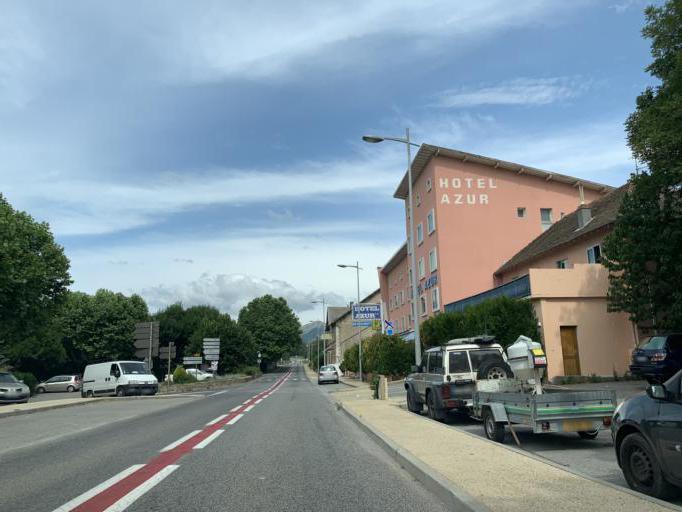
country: FR
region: Provence-Alpes-Cote d'Azur
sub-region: Departement des Hautes-Alpes
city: La Roche-des-Arnauds
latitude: 44.5414
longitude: 6.0137
